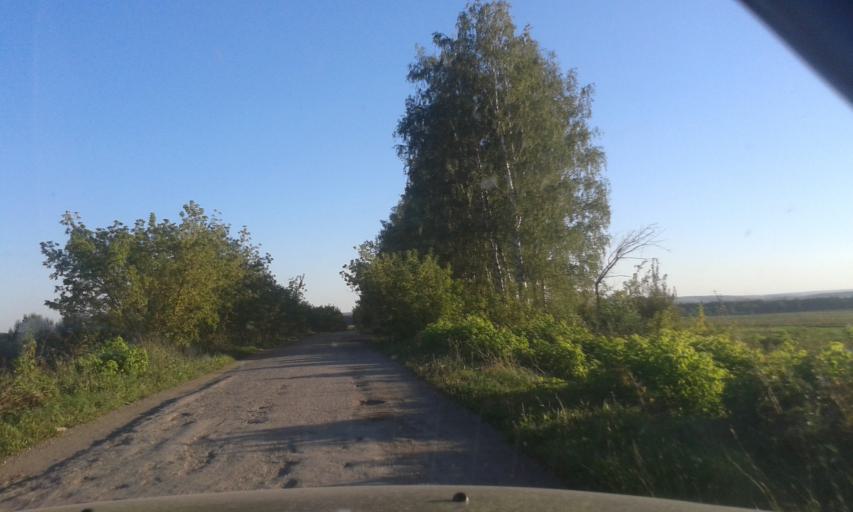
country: RU
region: Tula
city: Krapivna
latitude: 54.1287
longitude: 37.1562
